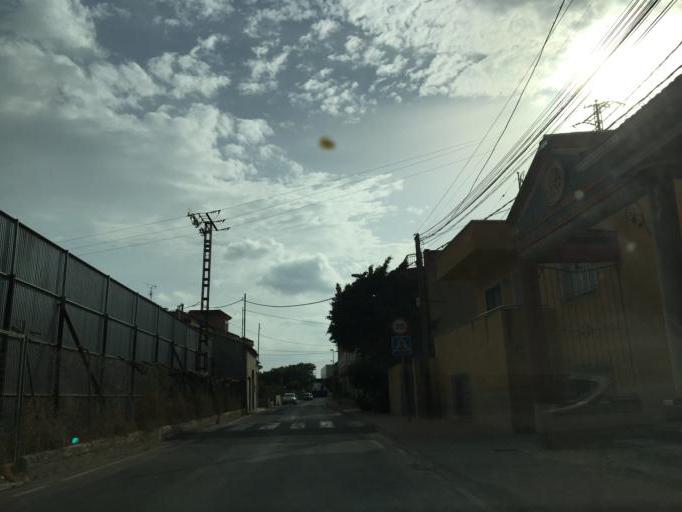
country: ES
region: Murcia
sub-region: Murcia
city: Murcia
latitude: 38.0143
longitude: -1.0978
